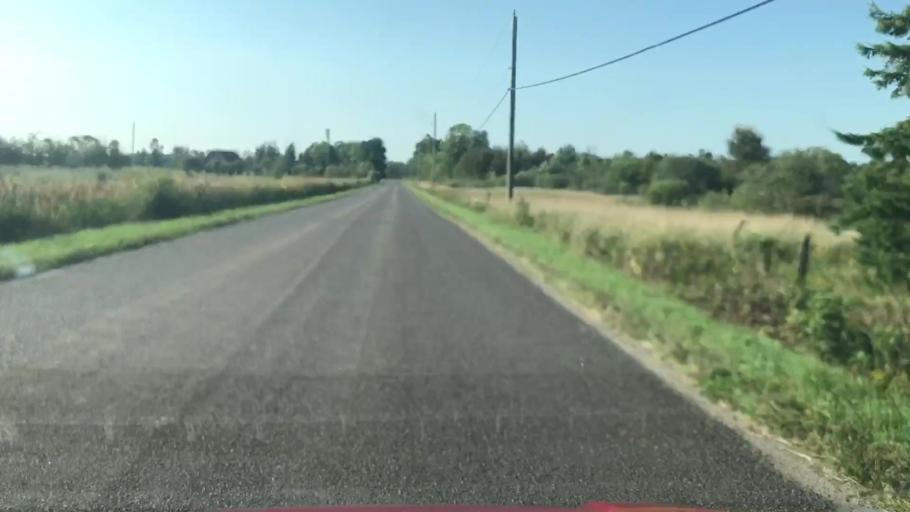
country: US
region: Michigan
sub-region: Chippewa County
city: Sault Ste. Marie
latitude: 46.2865
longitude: -84.0576
